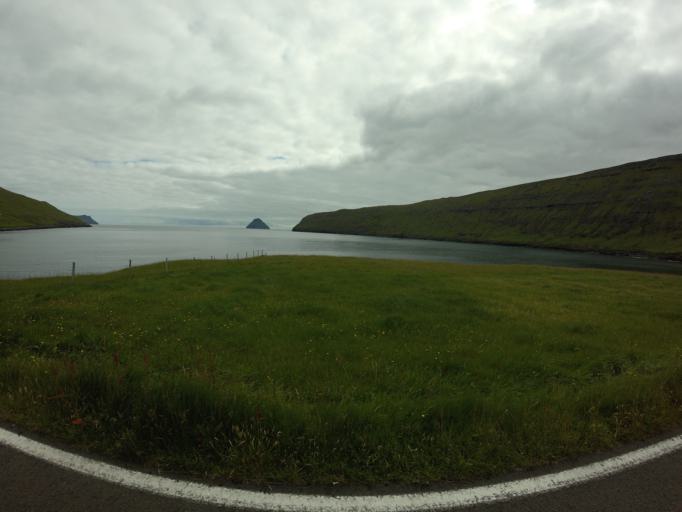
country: FO
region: Suduroy
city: Tvoroyri
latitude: 61.6308
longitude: -6.9294
